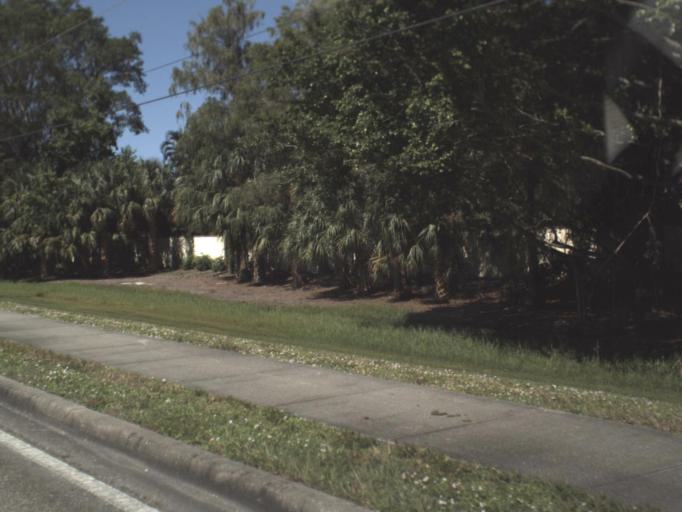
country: US
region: Florida
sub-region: Collier County
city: Lely
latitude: 26.1389
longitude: -81.7472
